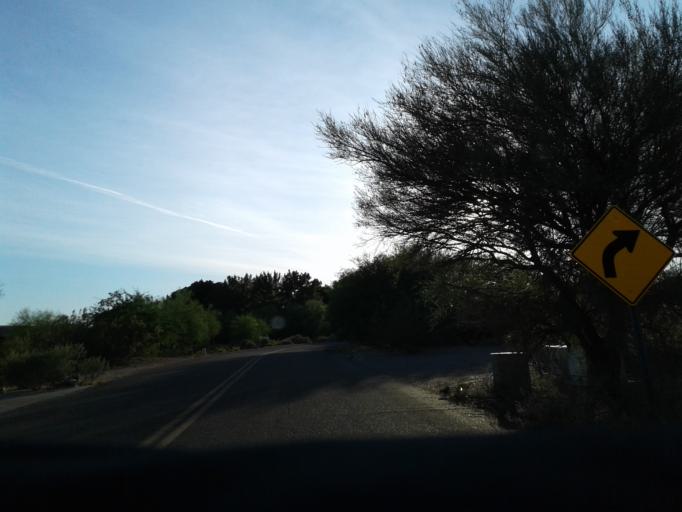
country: US
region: Arizona
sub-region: Maricopa County
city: Paradise Valley
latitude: 33.5270
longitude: -111.9993
